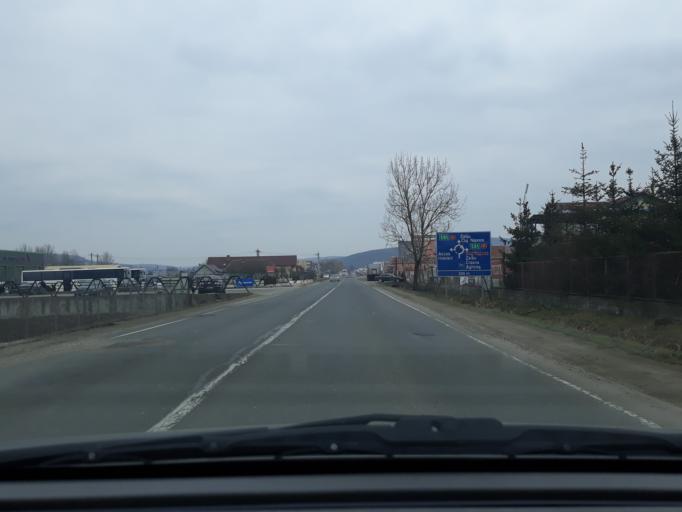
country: RO
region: Salaj
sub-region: Comuna Hereclean
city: Hereclean
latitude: 47.2248
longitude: 23.0172
